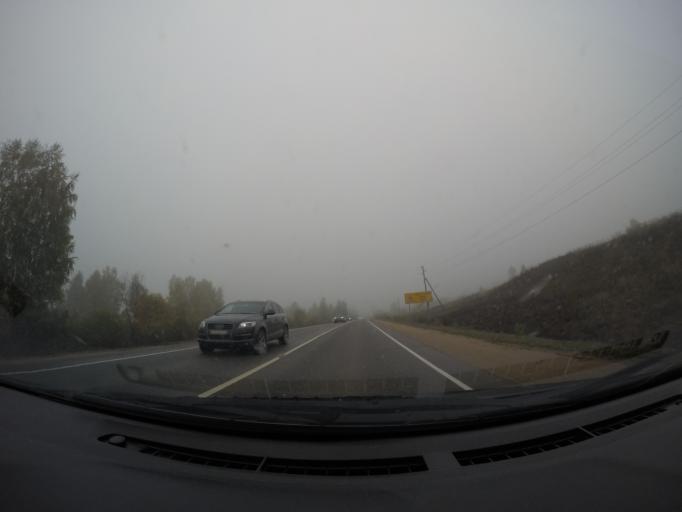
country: RU
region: Moskovskaya
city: Ruza
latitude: 55.7292
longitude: 36.3174
